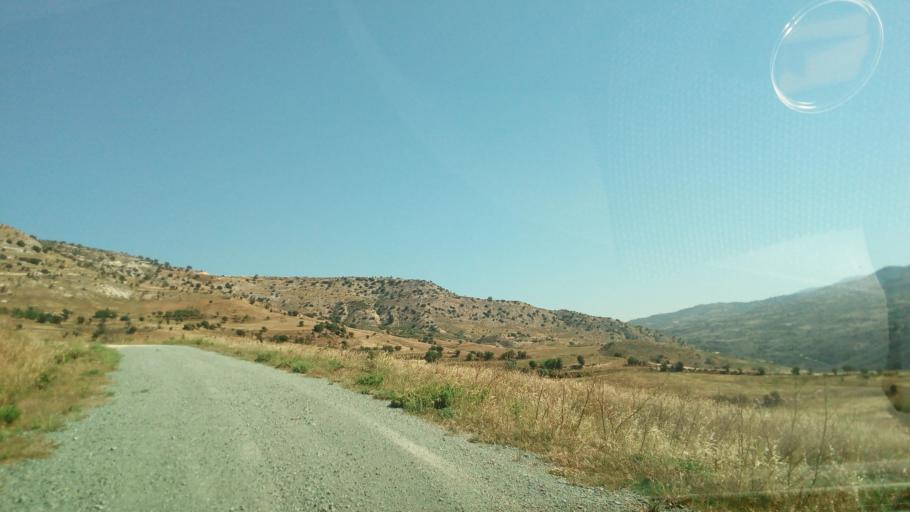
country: CY
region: Limassol
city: Pachna
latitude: 34.8168
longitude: 32.7088
